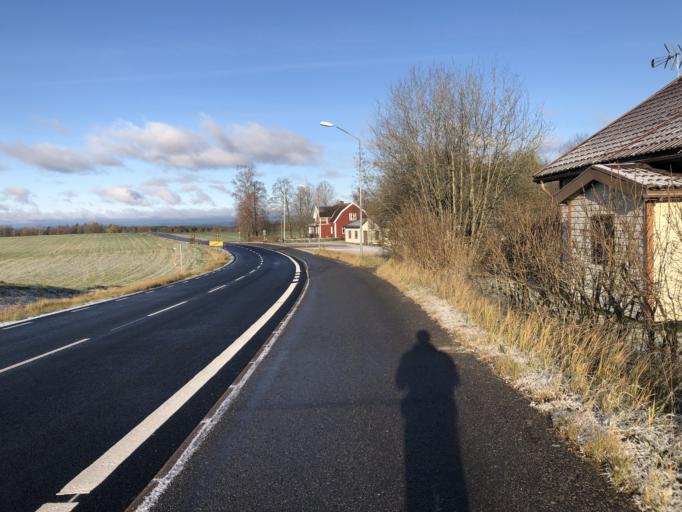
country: SE
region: Vaestra Goetaland
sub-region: Tranemo Kommun
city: Limmared
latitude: 57.6226
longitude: 13.4635
